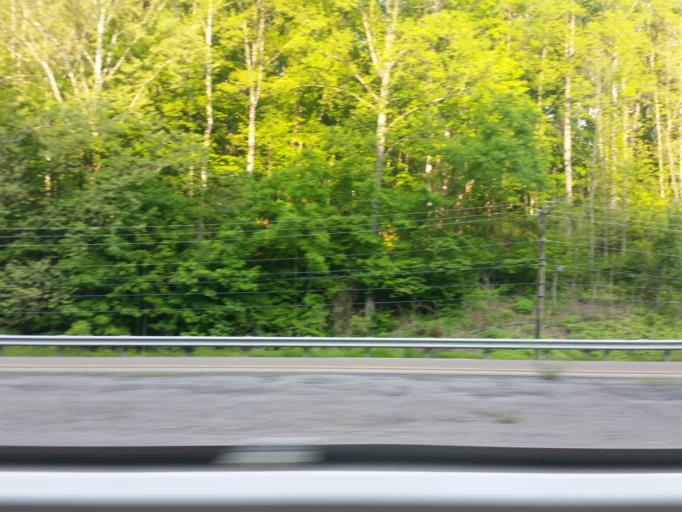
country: US
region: Virginia
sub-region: Russell County
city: Lebanon
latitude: 36.9182
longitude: -82.0061
